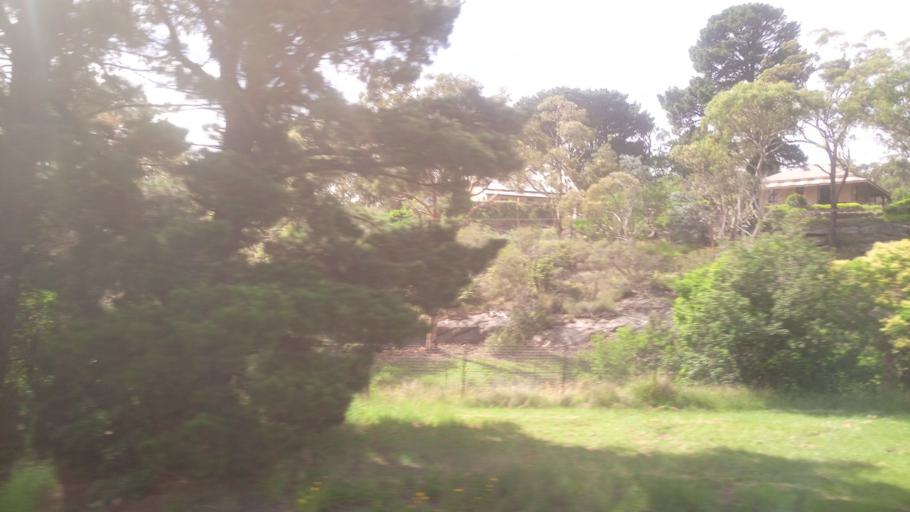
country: AU
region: New South Wales
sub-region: Blue Mountains Municipality
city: Hazelbrook
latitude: -33.7267
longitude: 150.4914
